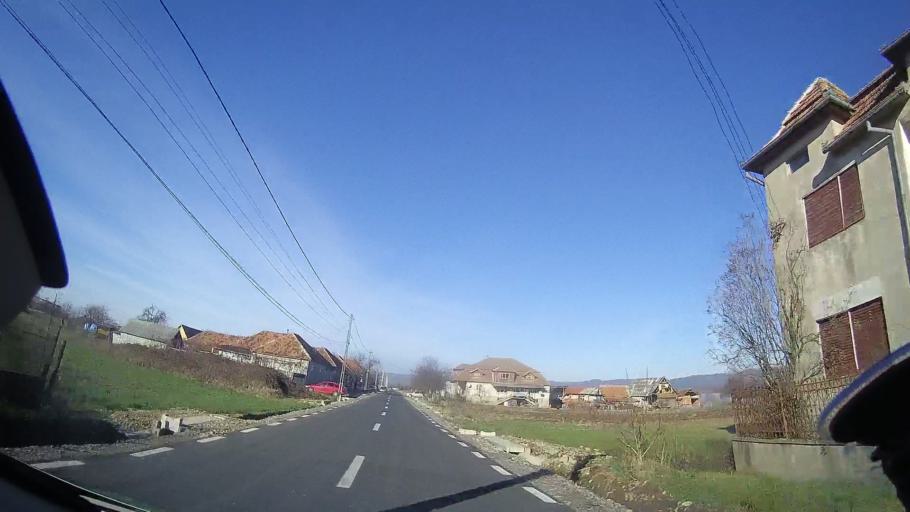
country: RO
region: Bihor
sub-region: Comuna Vadu Crisului
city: Vadu Crisului
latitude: 46.9918
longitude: 22.5091
